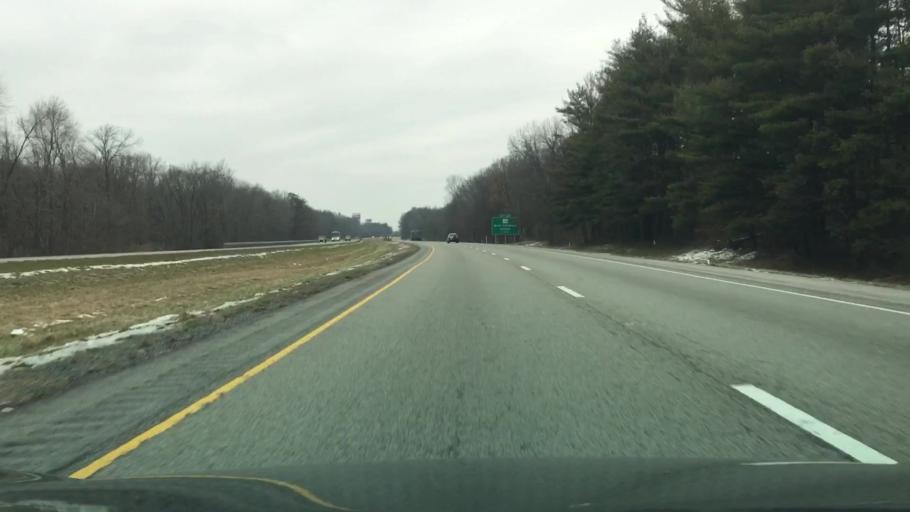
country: US
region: Illinois
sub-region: Franklin County
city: West Frankfort
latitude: 37.8792
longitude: -88.9415
